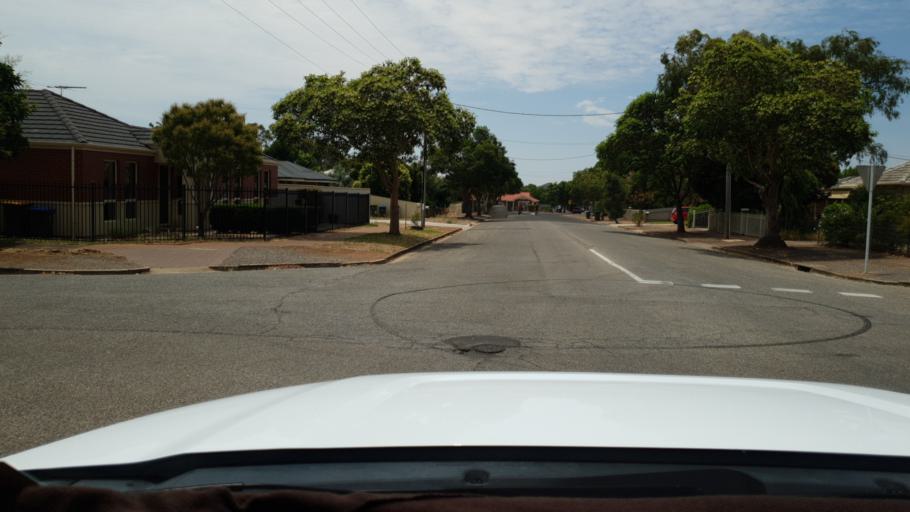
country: AU
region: South Australia
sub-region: Marion
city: Clovelly Park
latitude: -35.0020
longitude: 138.5791
